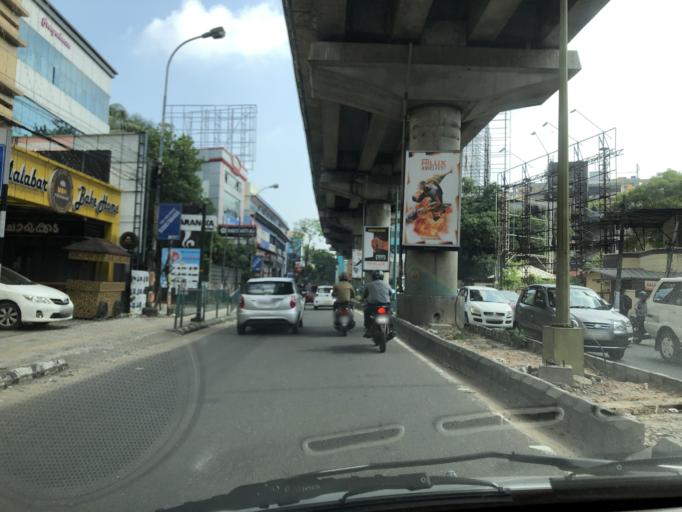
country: IN
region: Kerala
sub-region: Ernakulam
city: Elur
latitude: 9.9988
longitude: 76.2969
